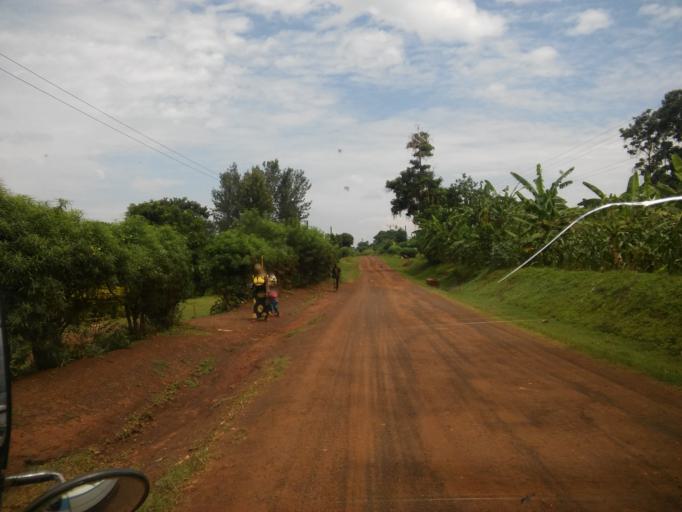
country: UG
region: Eastern Region
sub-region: Bududa District
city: Bududa
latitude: 0.9122
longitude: 34.2739
